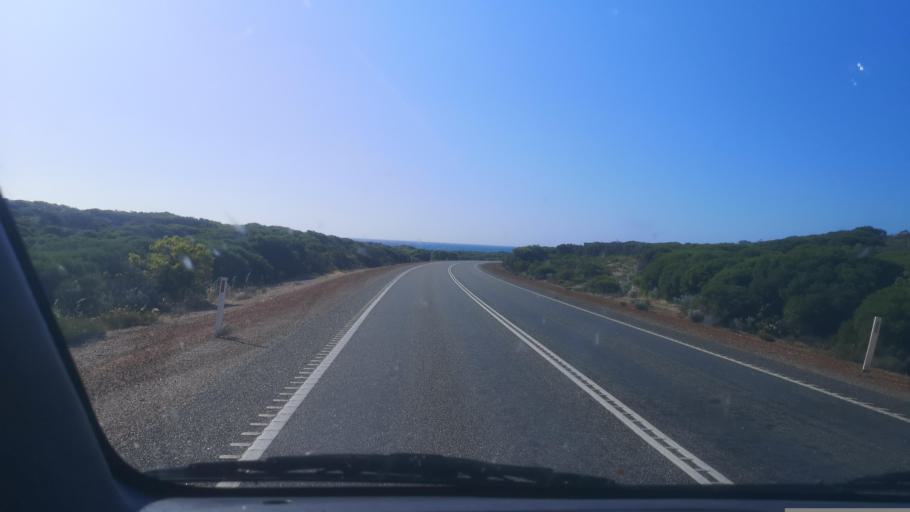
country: AU
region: Western Australia
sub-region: Dandaragan
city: Jurien Bay
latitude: -30.6623
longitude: 115.1416
